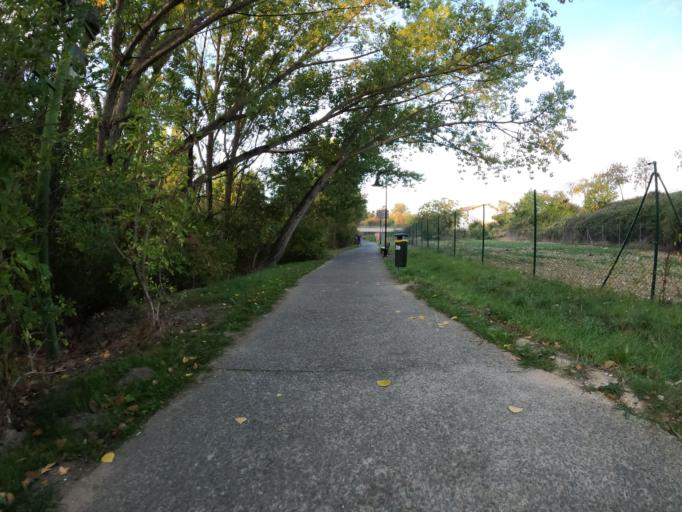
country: ES
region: Navarre
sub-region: Provincia de Navarra
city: Baranain
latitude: 42.8184
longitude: -1.6804
